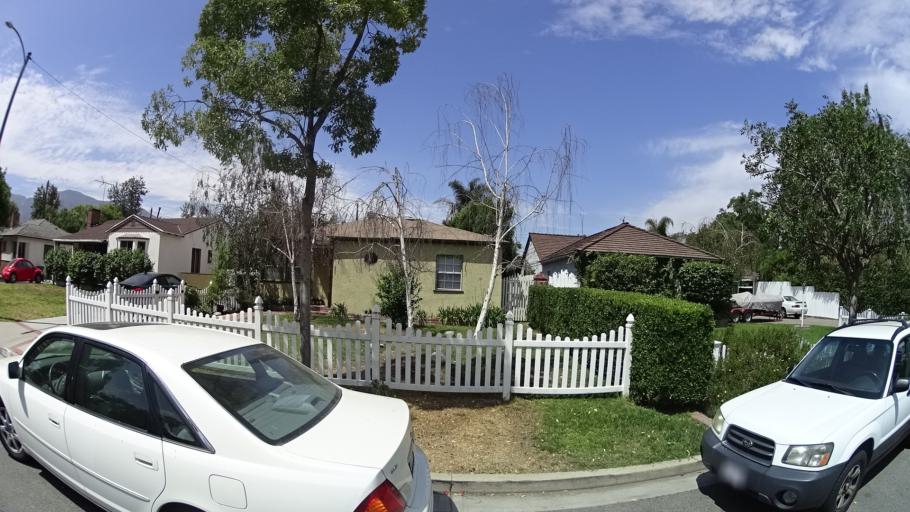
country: US
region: California
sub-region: Los Angeles County
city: Burbank
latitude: 34.1597
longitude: -118.3205
